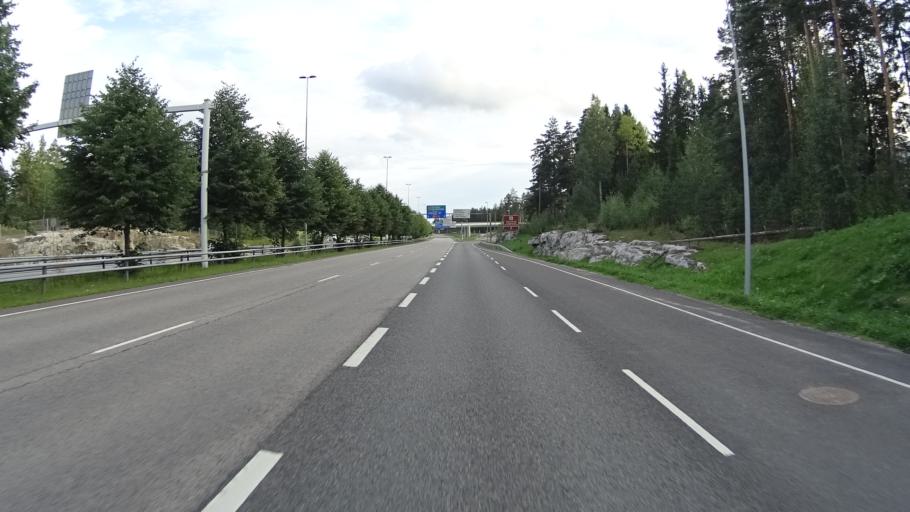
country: FI
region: Uusimaa
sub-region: Helsinki
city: Vantaa
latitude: 60.3046
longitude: 24.9631
